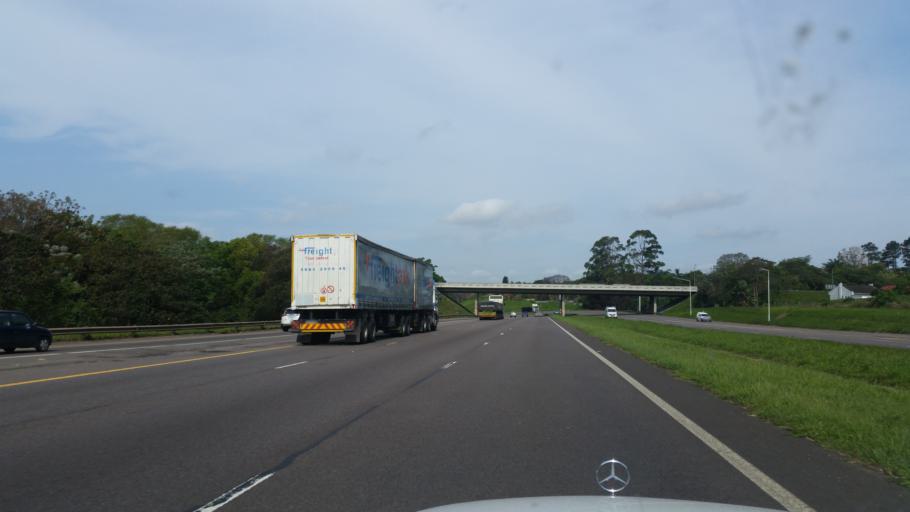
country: ZA
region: KwaZulu-Natal
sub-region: eThekwini Metropolitan Municipality
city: Berea
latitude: -29.8288
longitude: 30.8366
